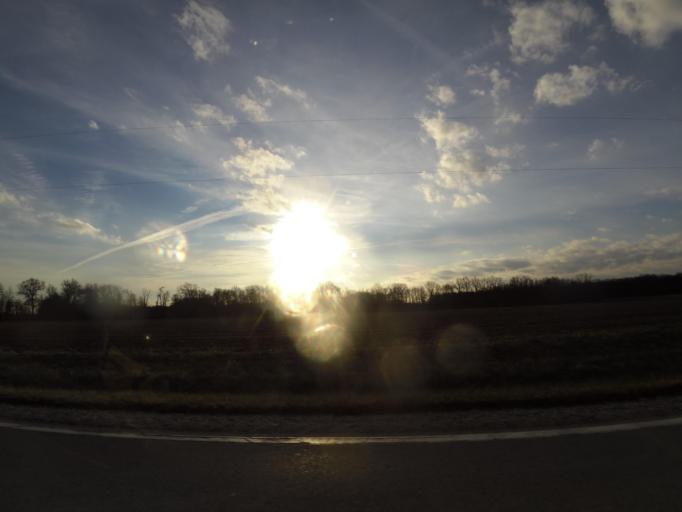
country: US
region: Illinois
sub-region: Fayette County
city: Vandalia
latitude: 38.9326
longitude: -89.1874
